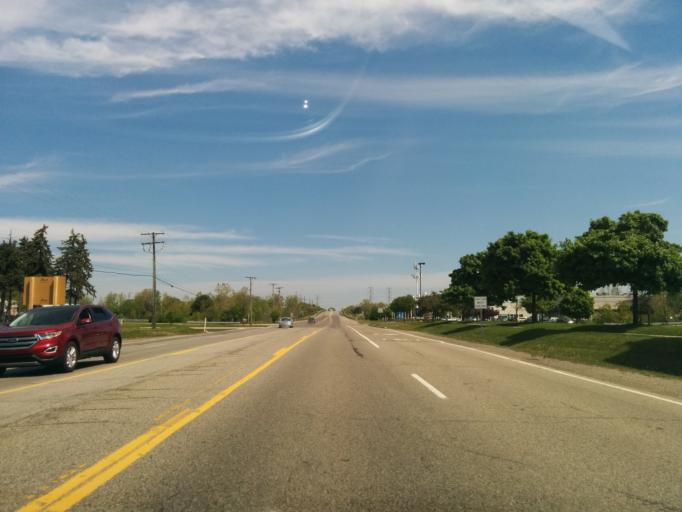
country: US
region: Michigan
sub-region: Oakland County
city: Novi
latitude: 42.4739
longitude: -83.4352
